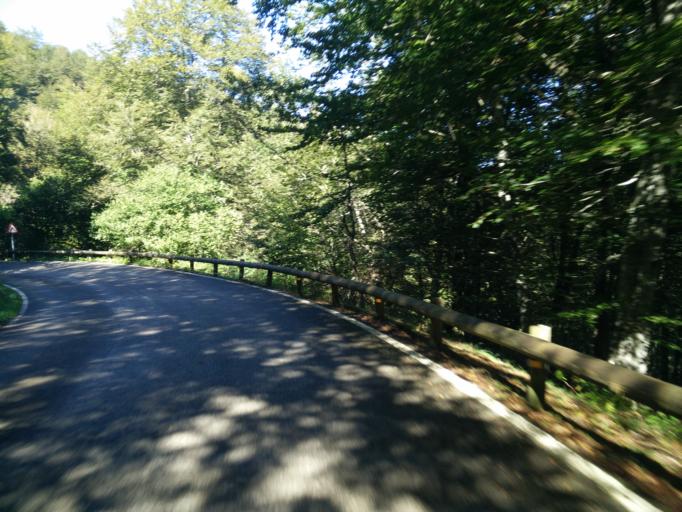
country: ES
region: Cantabria
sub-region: Provincia de Cantabria
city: Ruente
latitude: 43.1015
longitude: -4.2768
